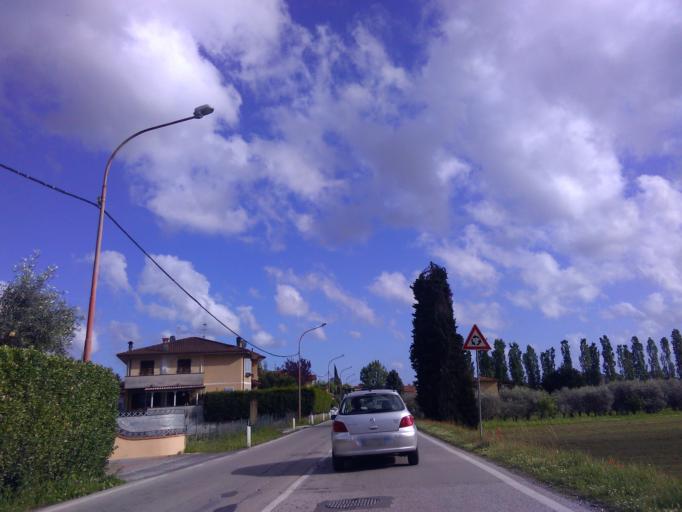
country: IT
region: Tuscany
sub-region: Provincia di Lucca
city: Ripa-Pozzi-Querceta-Ponterosso
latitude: 43.9676
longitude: 10.2210
